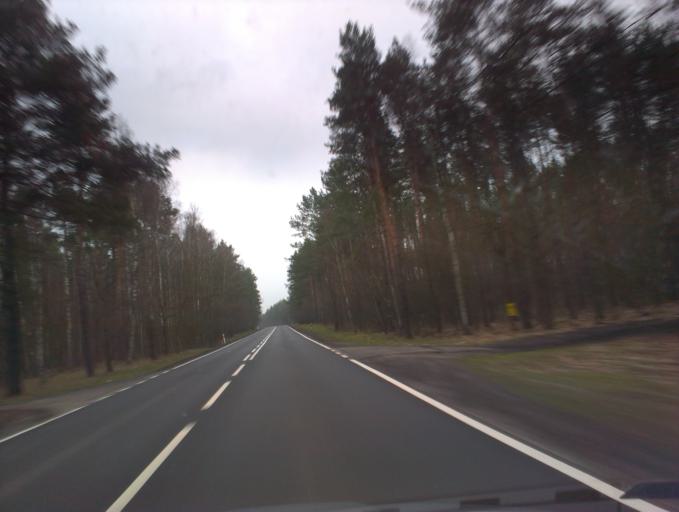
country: PL
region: Greater Poland Voivodeship
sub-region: Powiat pilski
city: Pila
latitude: 53.2036
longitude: 16.7788
